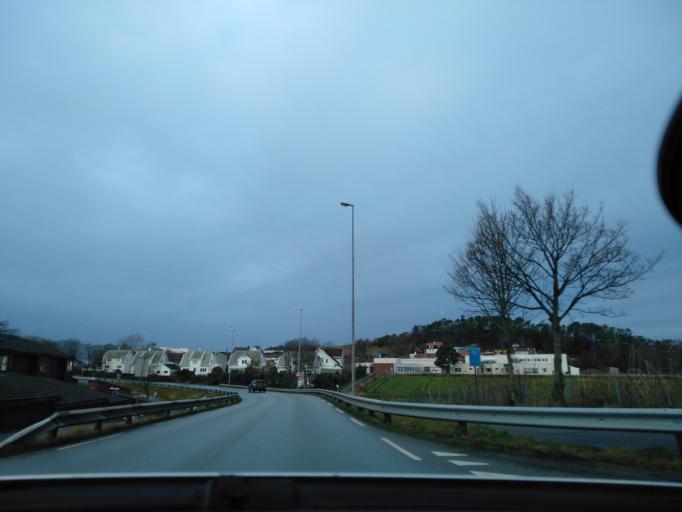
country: NO
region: Rogaland
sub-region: Randaberg
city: Randaberg
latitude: 58.9979
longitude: 5.6256
